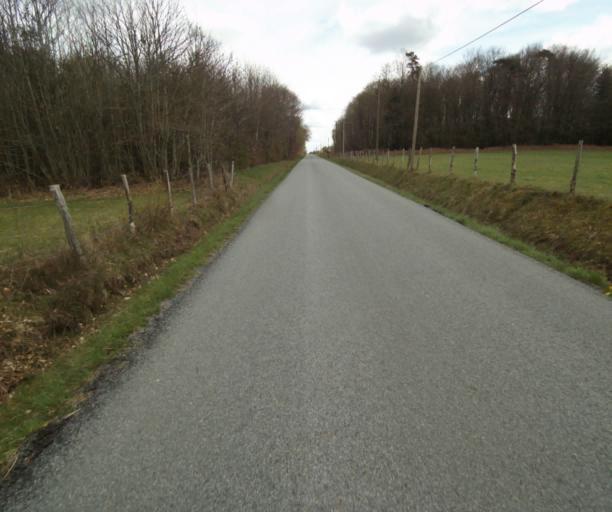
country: FR
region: Limousin
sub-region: Departement de la Correze
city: Laguenne
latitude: 45.2057
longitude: 1.8860
